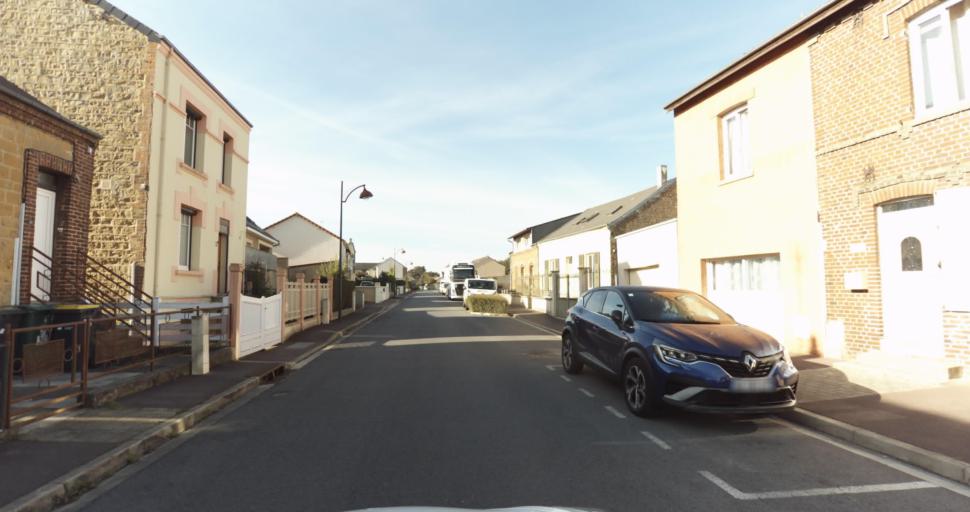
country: FR
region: Champagne-Ardenne
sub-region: Departement des Ardennes
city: Villers-Semeuse
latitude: 49.7468
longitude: 4.7393
